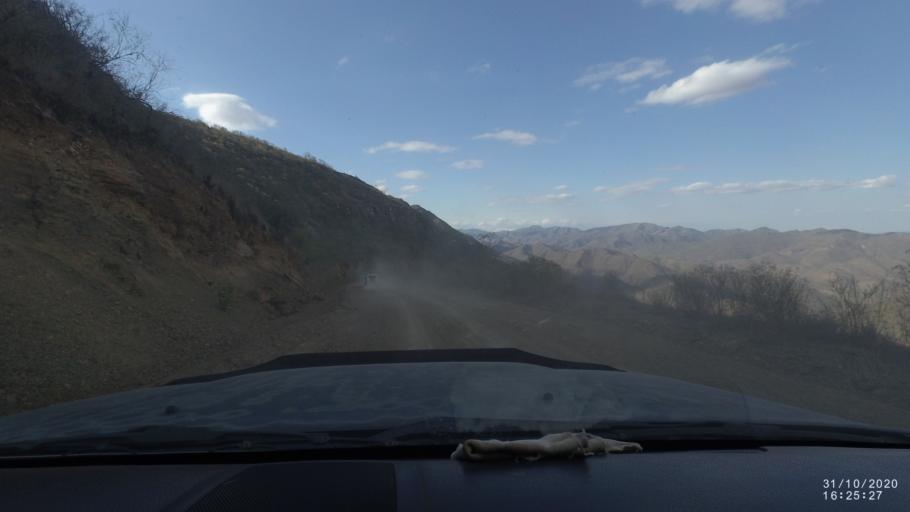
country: BO
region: Chuquisaca
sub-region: Provincia Zudanez
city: Mojocoya
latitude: -18.4008
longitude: -64.5873
